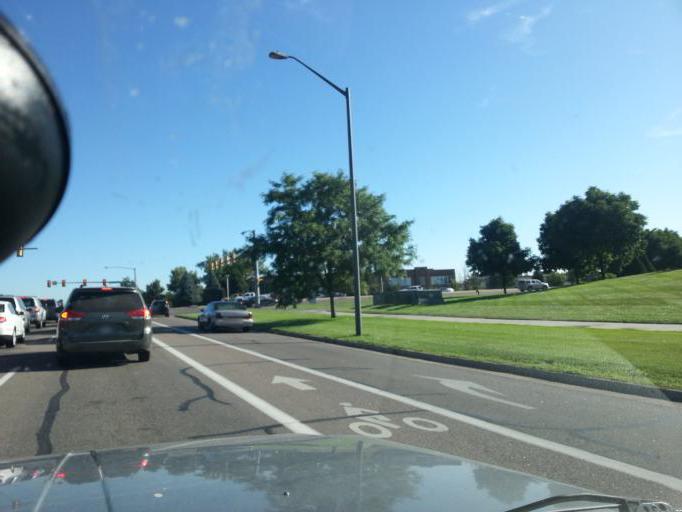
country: US
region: Colorado
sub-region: Larimer County
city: Fort Collins
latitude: 40.5224
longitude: -105.0392
